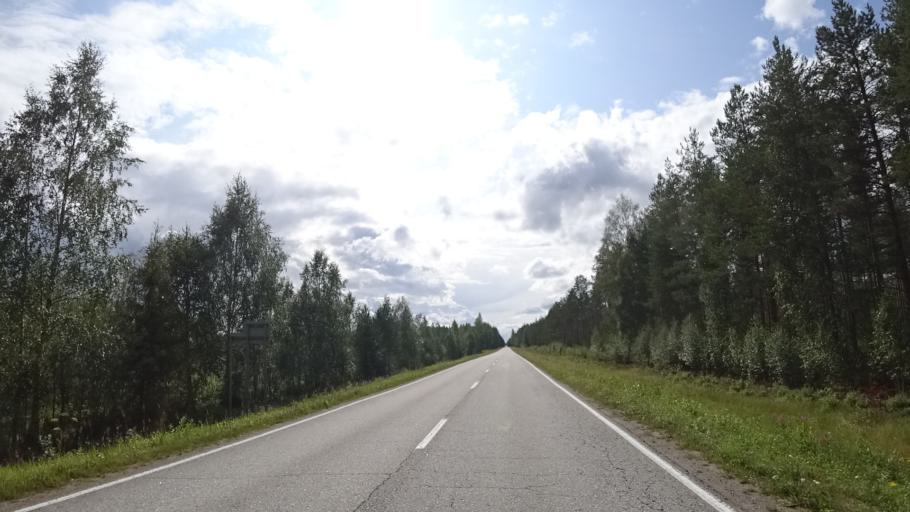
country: FI
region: North Karelia
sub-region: Joensuu
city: Ilomantsi
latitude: 62.7646
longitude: 31.0276
